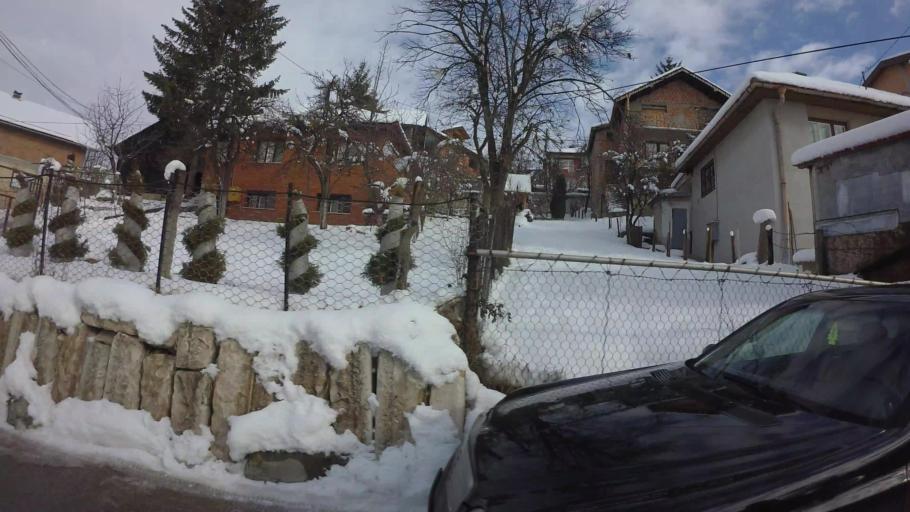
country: BA
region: Federation of Bosnia and Herzegovina
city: Kobilja Glava
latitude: 43.8766
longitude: 18.4177
